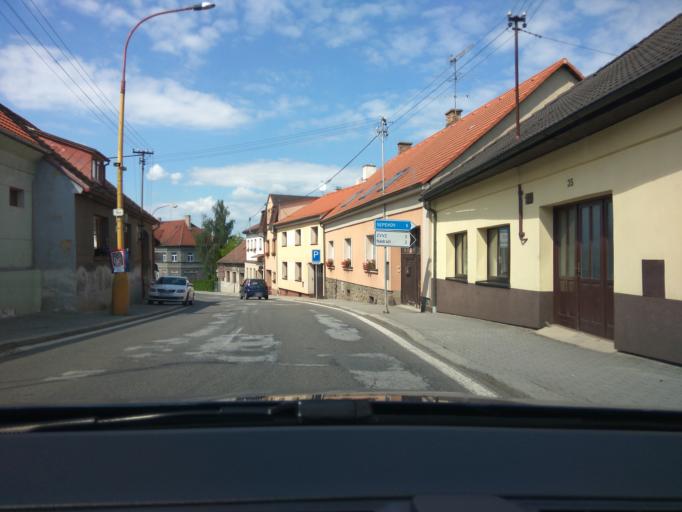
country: CZ
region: Jihocesky
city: Milevsko
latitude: 49.4464
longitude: 14.3604
